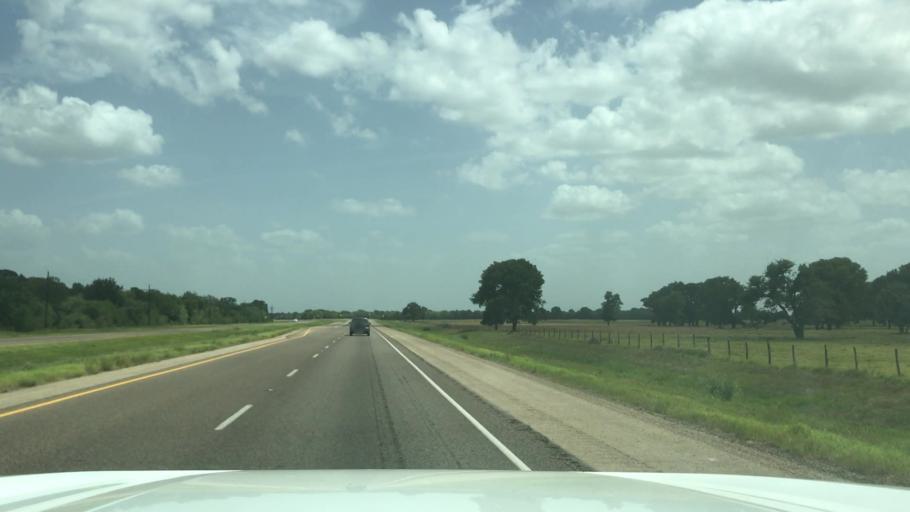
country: US
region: Texas
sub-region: Robertson County
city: Calvert
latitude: 30.9994
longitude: -96.6939
